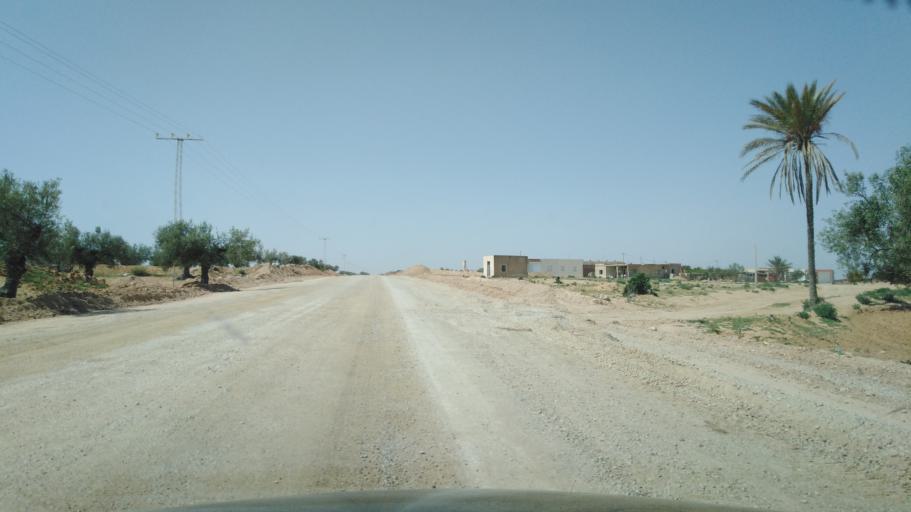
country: TN
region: Safaqis
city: Sfax
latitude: 34.6847
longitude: 10.4601
